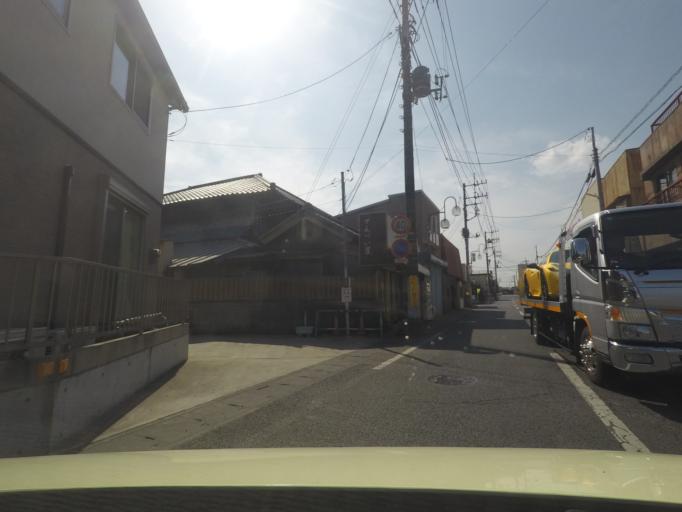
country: JP
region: Ibaraki
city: Ishioka
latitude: 36.1704
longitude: 140.3533
